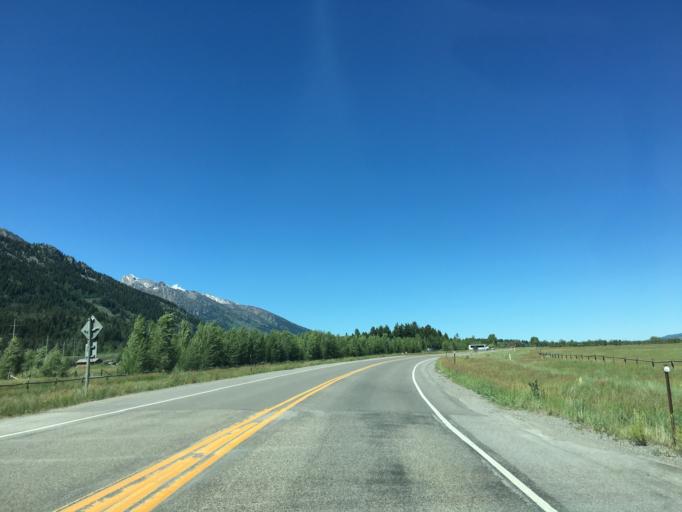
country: US
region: Wyoming
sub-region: Teton County
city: Moose Wilson Road
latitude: 43.5838
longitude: -110.8215
